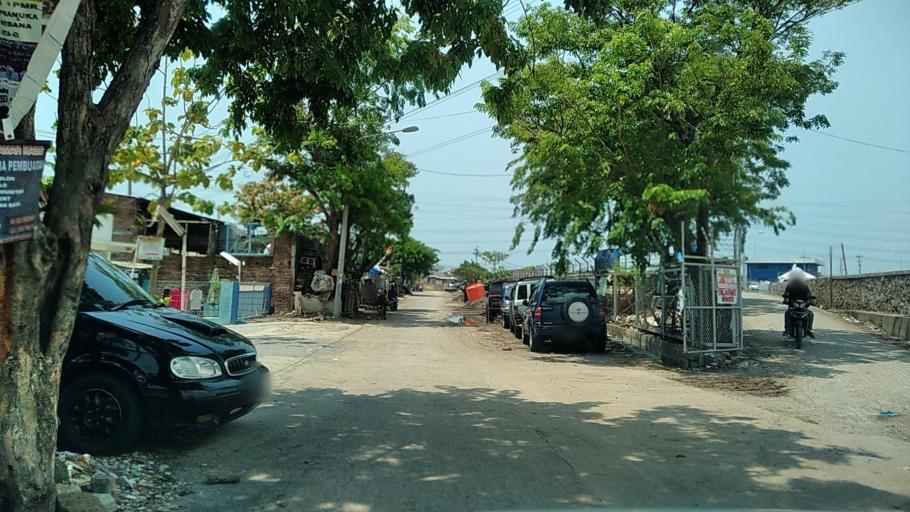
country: ID
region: Central Java
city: Semarang
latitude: -6.9530
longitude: 110.4398
